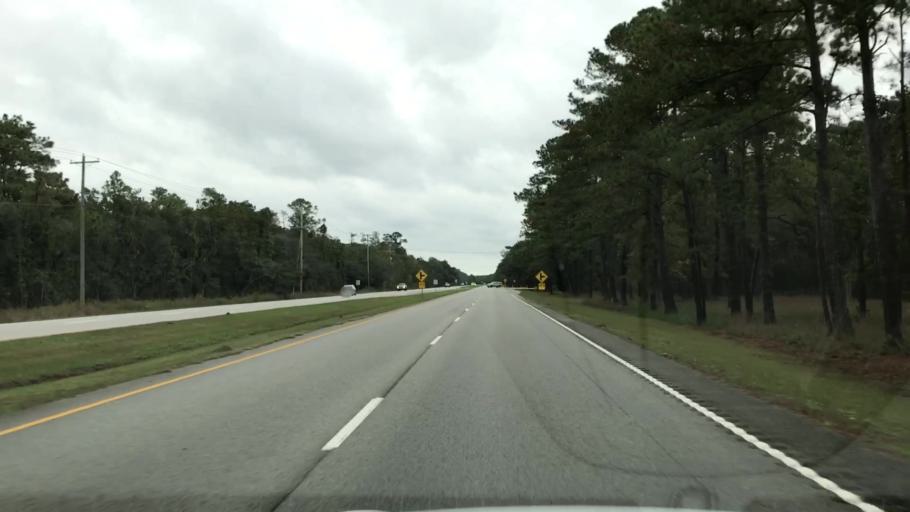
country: US
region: South Carolina
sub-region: Georgetown County
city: Georgetown
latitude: 33.3735
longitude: -79.2155
